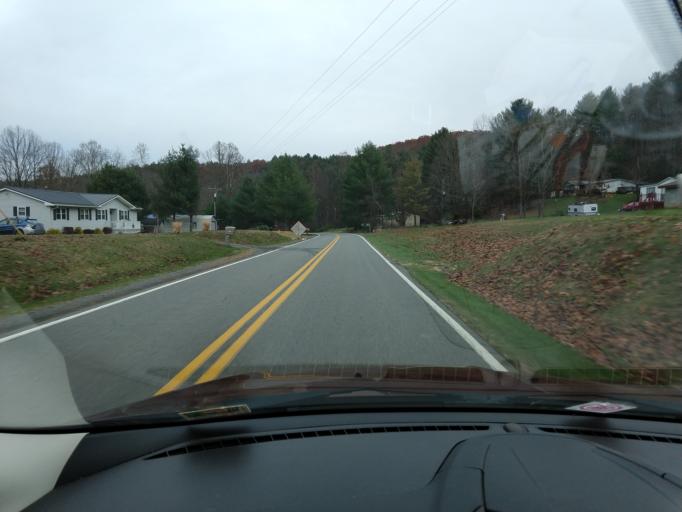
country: US
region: West Virginia
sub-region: Greenbrier County
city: White Sulphur Springs
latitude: 37.7407
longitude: -80.1767
